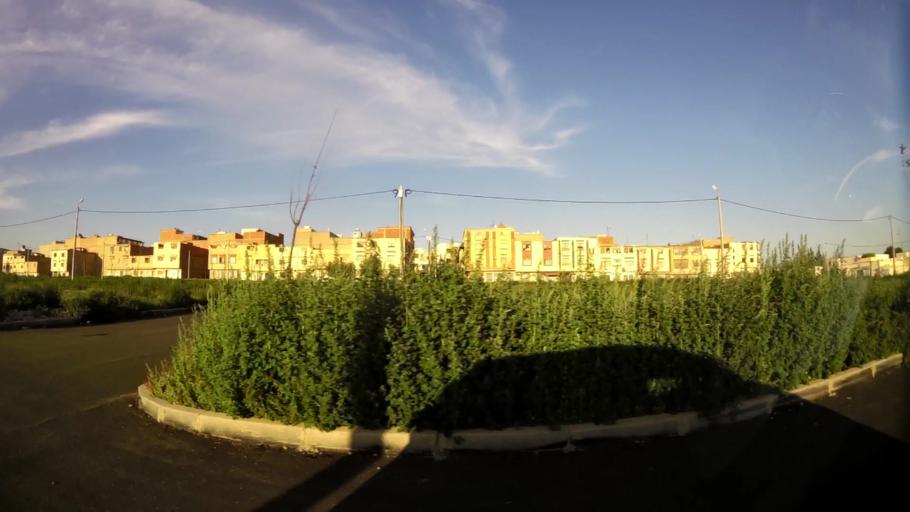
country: MA
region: Oriental
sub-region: Oujda-Angad
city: Oujda
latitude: 34.6985
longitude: -1.9178
